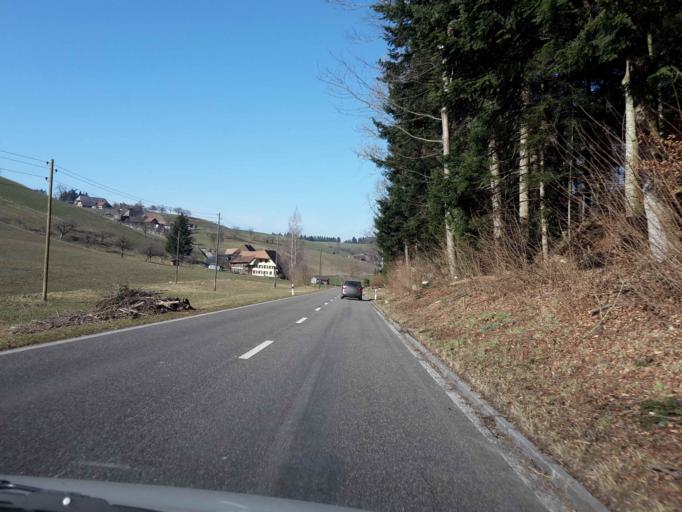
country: CH
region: Bern
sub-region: Emmental District
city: Durrenroth
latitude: 47.1051
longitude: 7.7761
